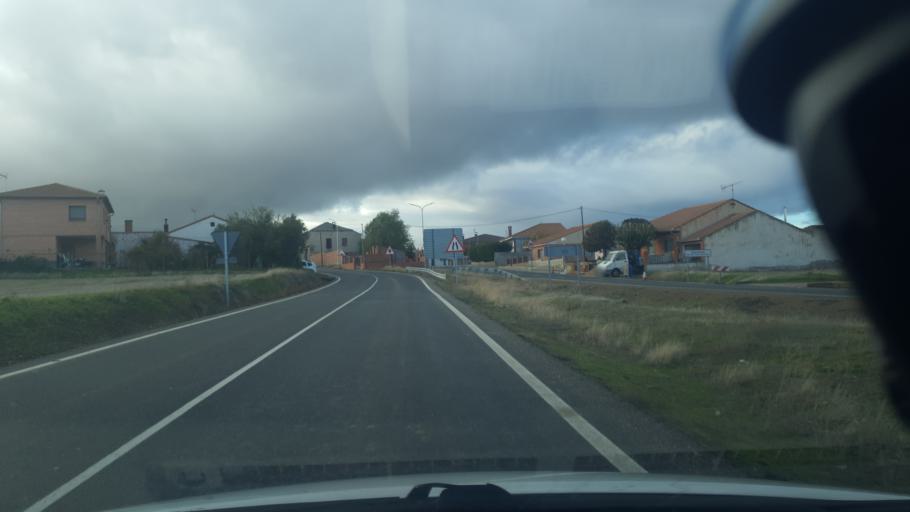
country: ES
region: Castille and Leon
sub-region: Provincia de Segovia
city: Santiuste de San Juan Bautista
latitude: 41.1548
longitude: -4.5680
